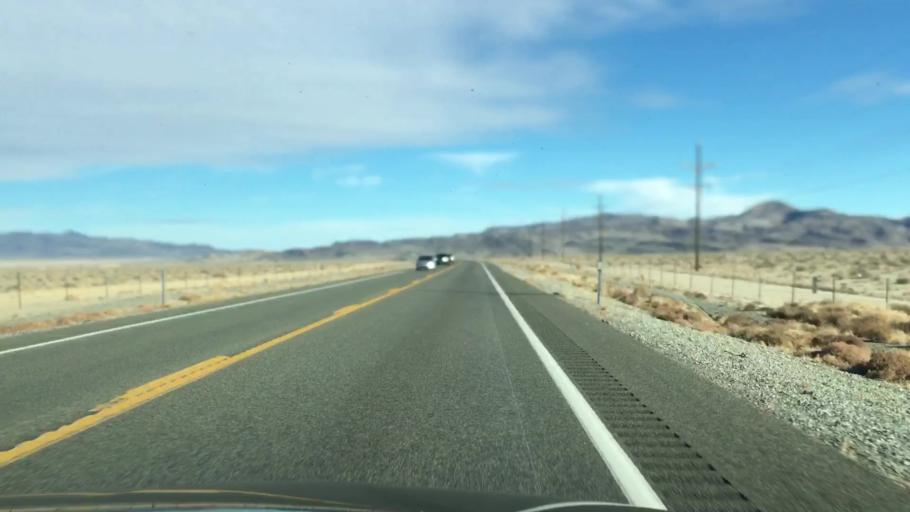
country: US
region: Nevada
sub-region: Mineral County
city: Hawthorne
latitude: 38.5246
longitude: -118.5828
